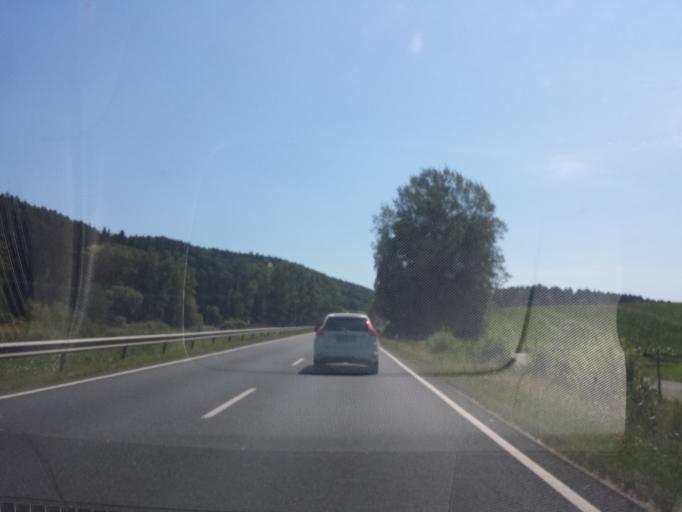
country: DE
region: Bavaria
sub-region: Upper Palatinate
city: Traitsching
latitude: 49.1438
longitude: 12.6490
